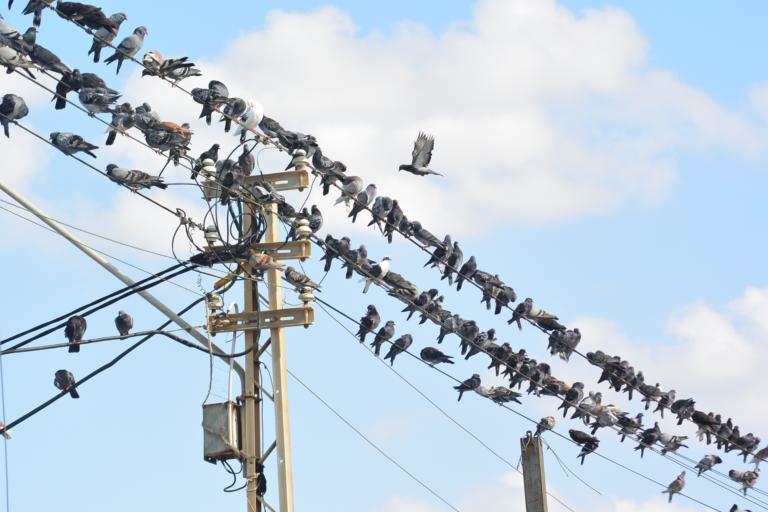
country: IL
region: Tel Aviv
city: Tel Aviv
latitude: 32.0674
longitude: 34.7666
